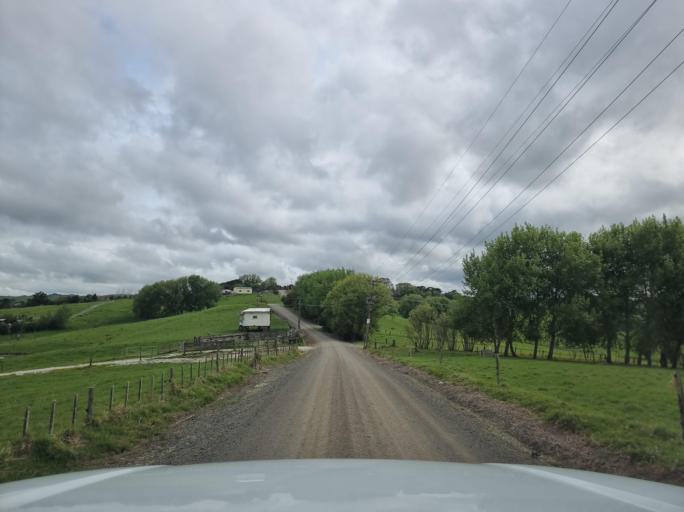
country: NZ
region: Northland
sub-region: Whangarei
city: Ruakaka
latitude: -36.1301
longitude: 174.2084
